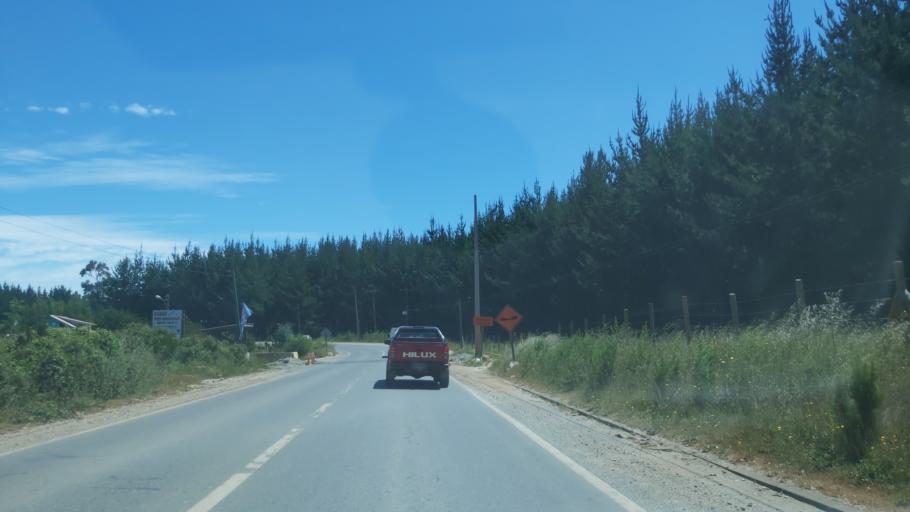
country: CL
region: Maule
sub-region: Provincia de Talca
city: Constitucion
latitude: -35.3984
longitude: -72.4346
